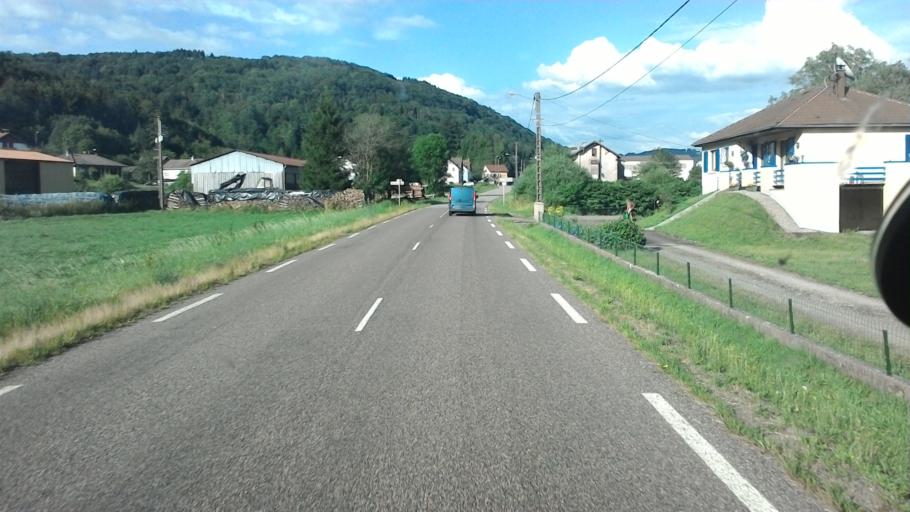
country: FR
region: Lorraine
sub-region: Departement des Vosges
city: Rupt-sur-Moselle
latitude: 47.8803
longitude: 6.5834
